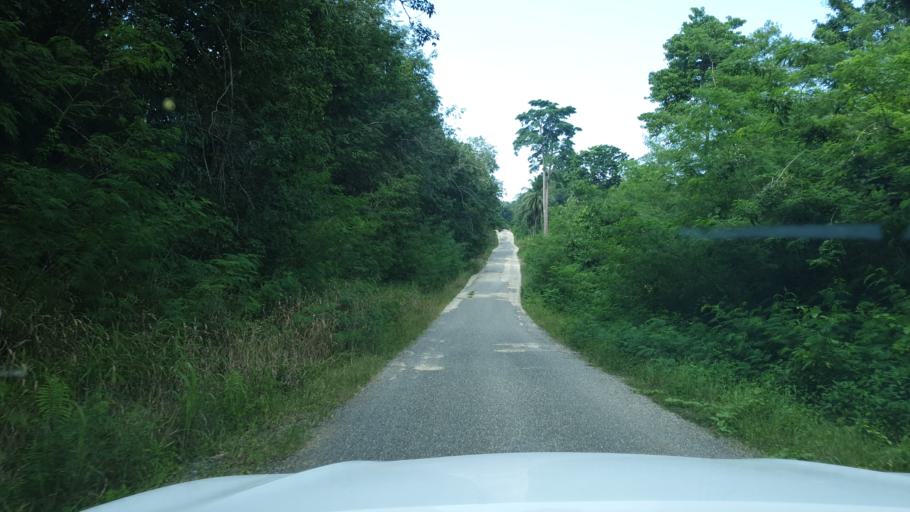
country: PG
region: East Sepik
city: Angoram
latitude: -3.9582
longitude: 144.0349
